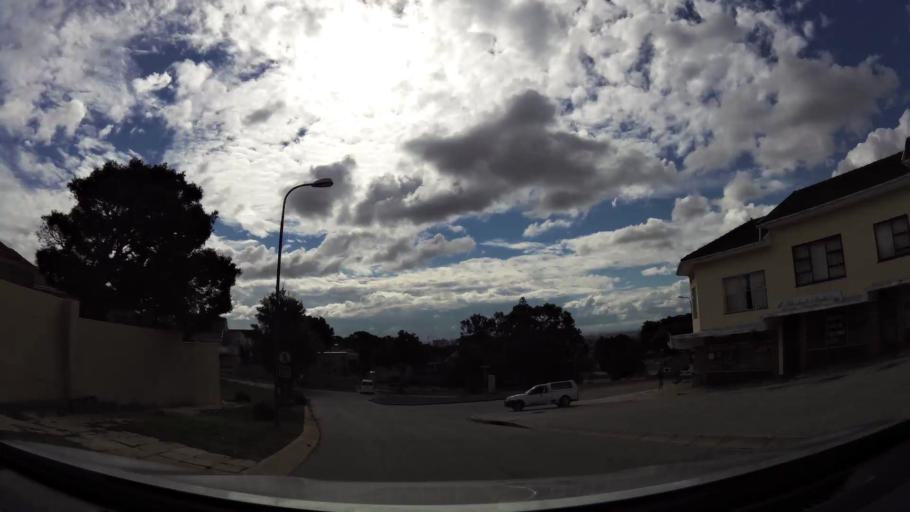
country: ZA
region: Eastern Cape
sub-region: Nelson Mandela Bay Metropolitan Municipality
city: Port Elizabeth
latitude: -33.9428
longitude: 25.5853
